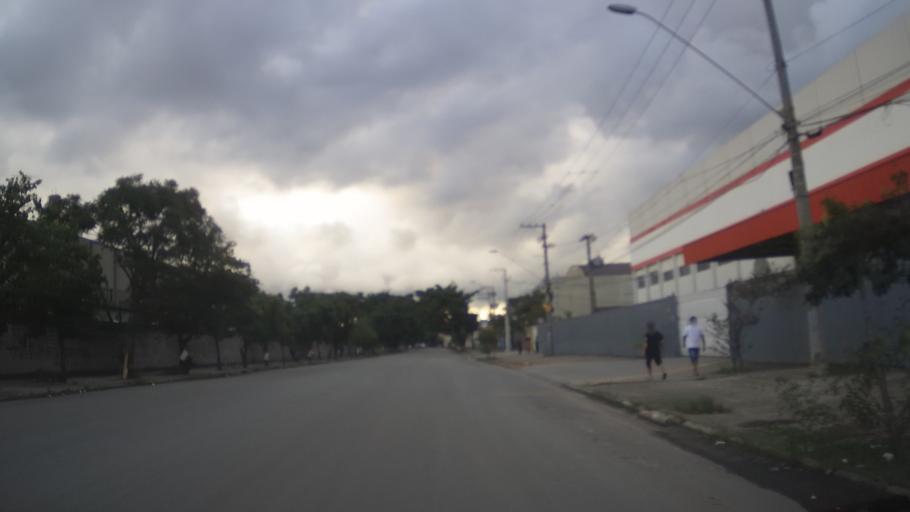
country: BR
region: Sao Paulo
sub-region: Guarulhos
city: Guarulhos
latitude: -23.4735
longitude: -46.4621
